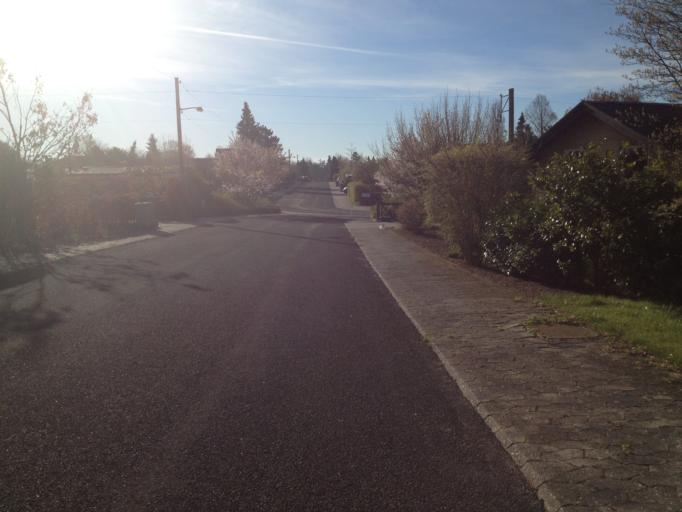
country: DK
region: Capital Region
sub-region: Ballerup Kommune
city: Ballerup
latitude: 55.7527
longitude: 12.3886
